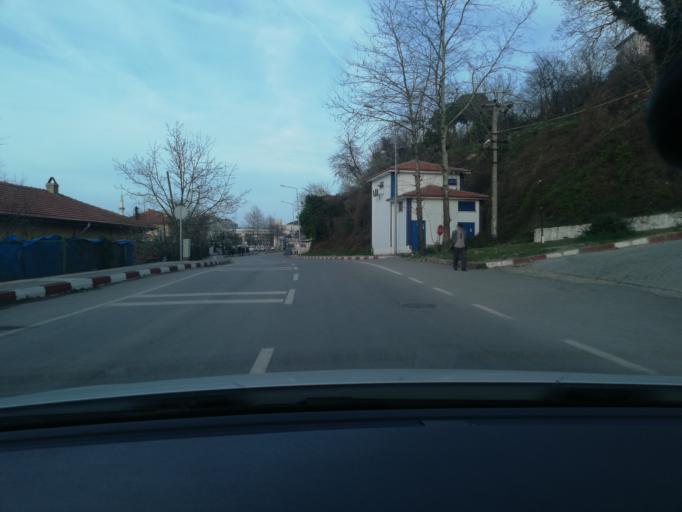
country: TR
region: Zonguldak
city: Tieum
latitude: 41.5590
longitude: 32.0205
